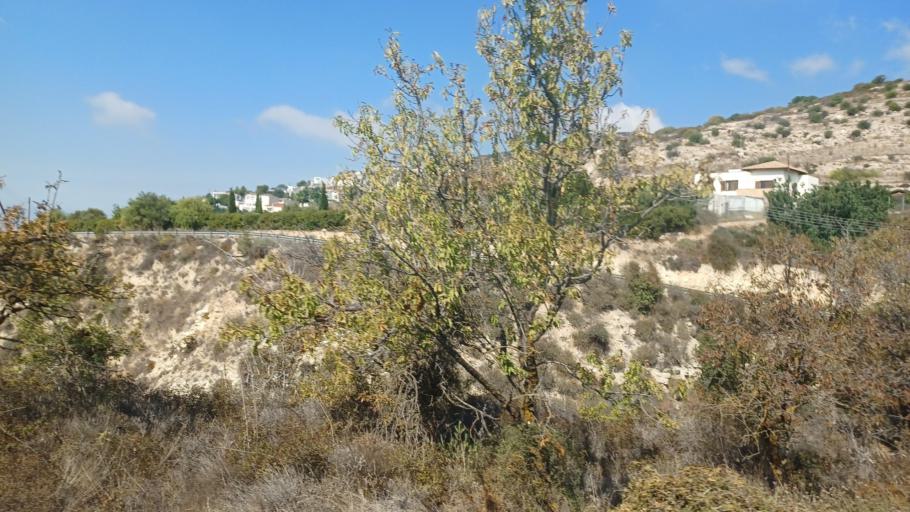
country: CY
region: Pafos
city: Mesogi
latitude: 34.8340
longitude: 32.4566
